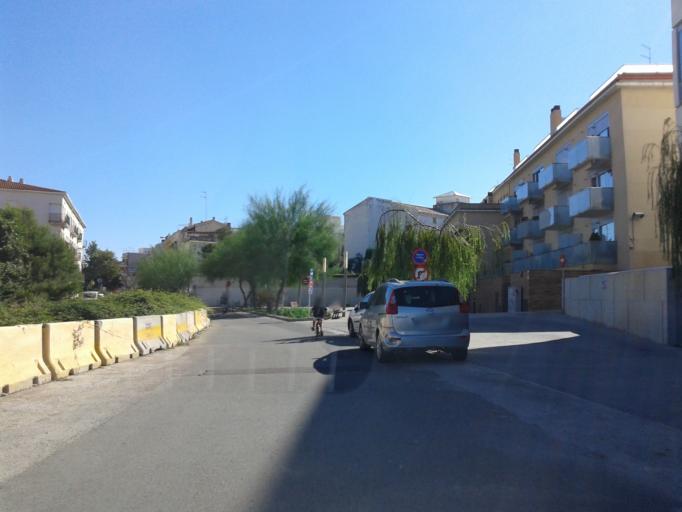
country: ES
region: Catalonia
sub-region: Provincia de Barcelona
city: Vilanova i la Geltru
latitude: 41.2290
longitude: 1.7239
